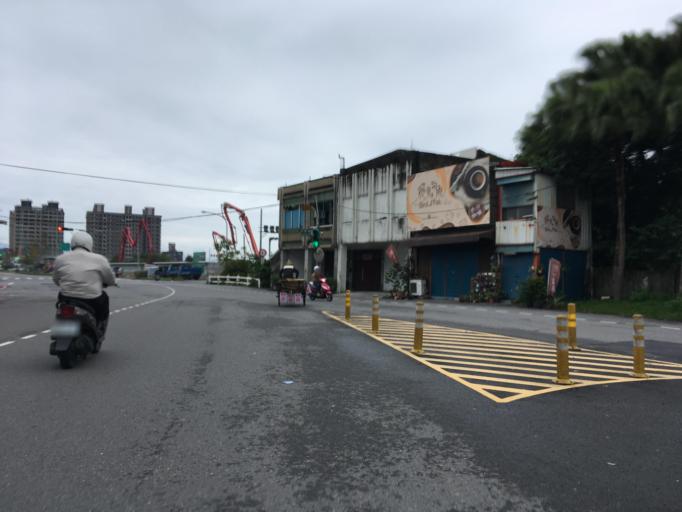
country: TW
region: Taiwan
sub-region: Yilan
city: Yilan
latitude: 24.6854
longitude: 121.7709
